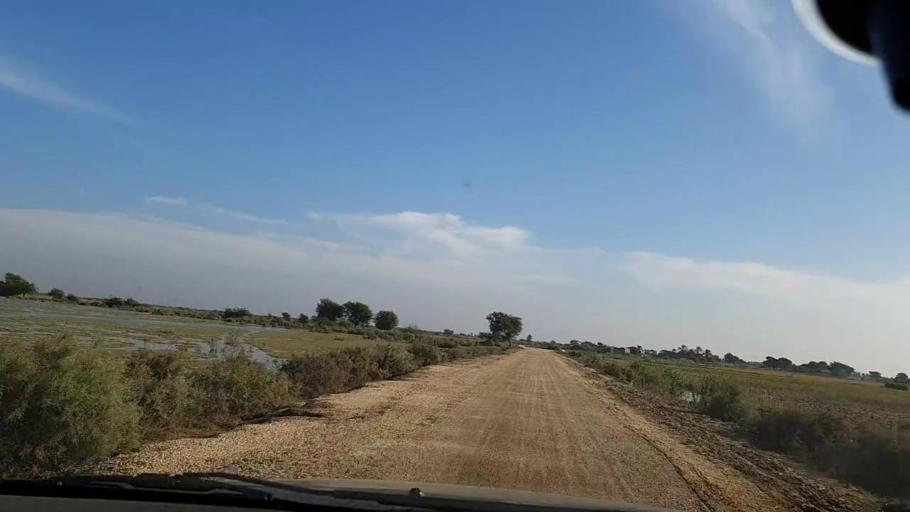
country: PK
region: Sindh
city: Mirpur Batoro
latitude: 24.6569
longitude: 68.3085
